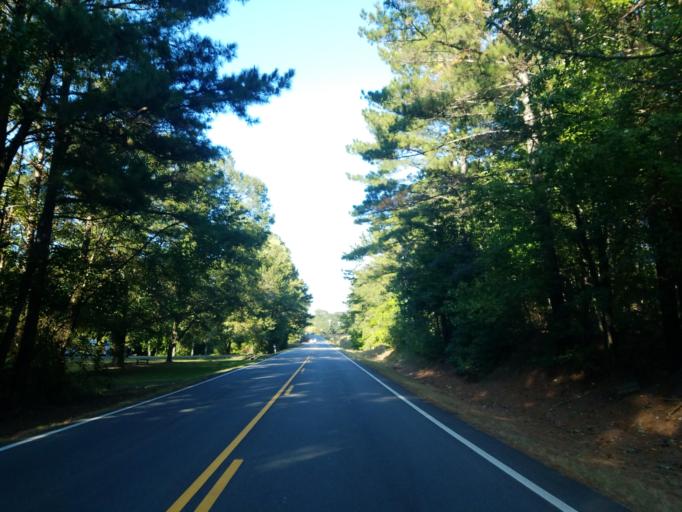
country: US
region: Georgia
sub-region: Bartow County
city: Emerson
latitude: 34.0505
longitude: -84.8314
